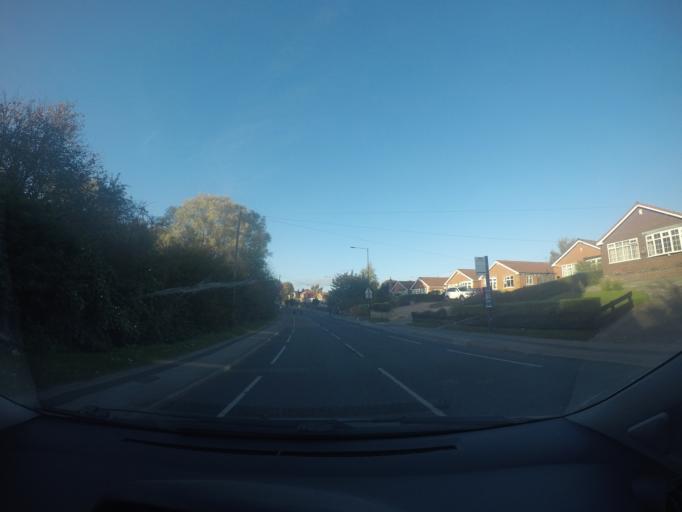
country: GB
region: England
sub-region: City of York
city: Huntington
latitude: 53.9812
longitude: -1.0674
